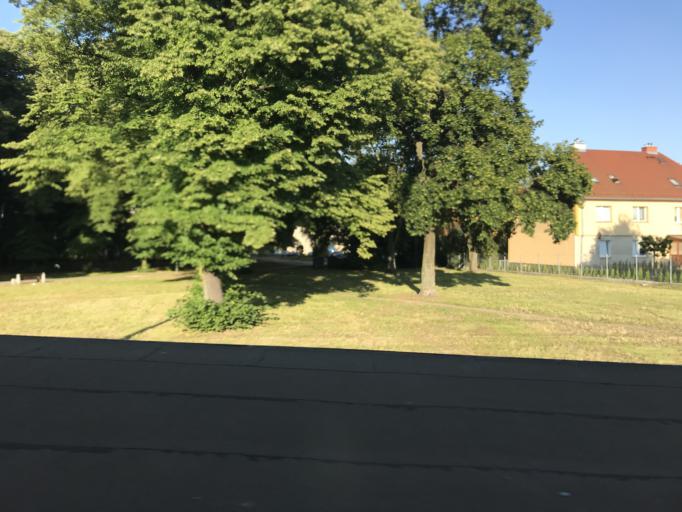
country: PL
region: Pomeranian Voivodeship
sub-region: Gdansk
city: Gdansk
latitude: 54.3215
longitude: 18.6337
